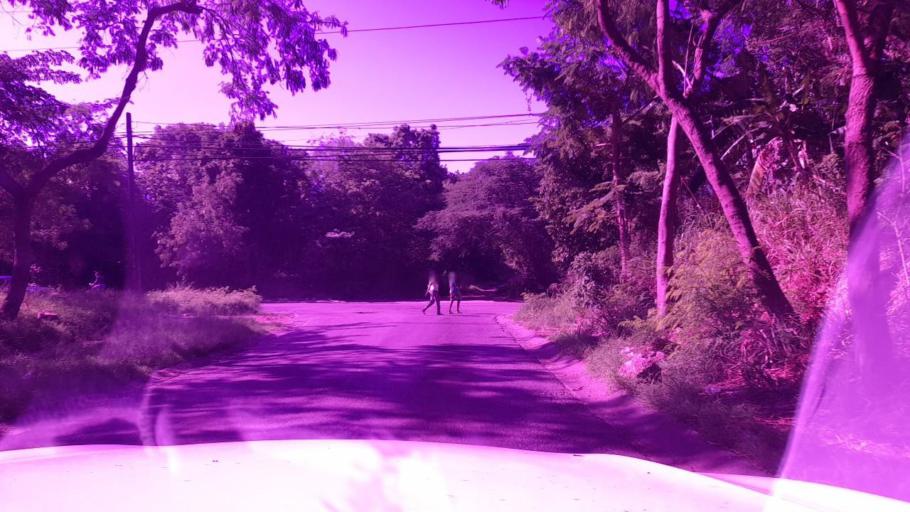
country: CU
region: La Habana
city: Alamar
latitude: 23.1625
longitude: -82.2769
